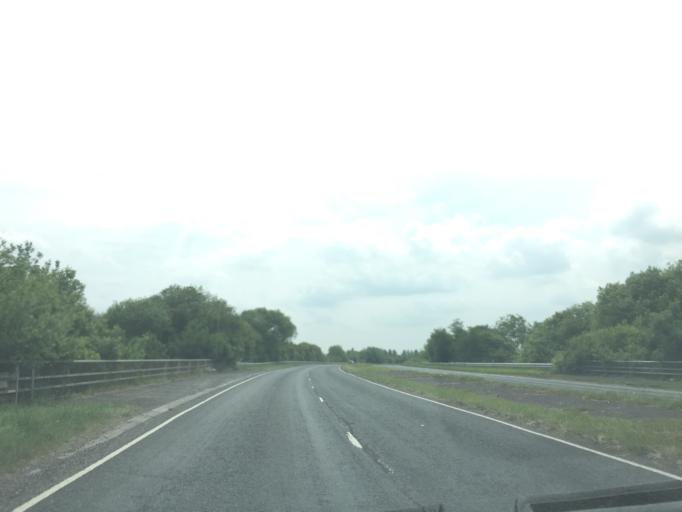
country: GB
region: England
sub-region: Hampshire
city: Alton
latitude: 51.1443
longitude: -0.9593
